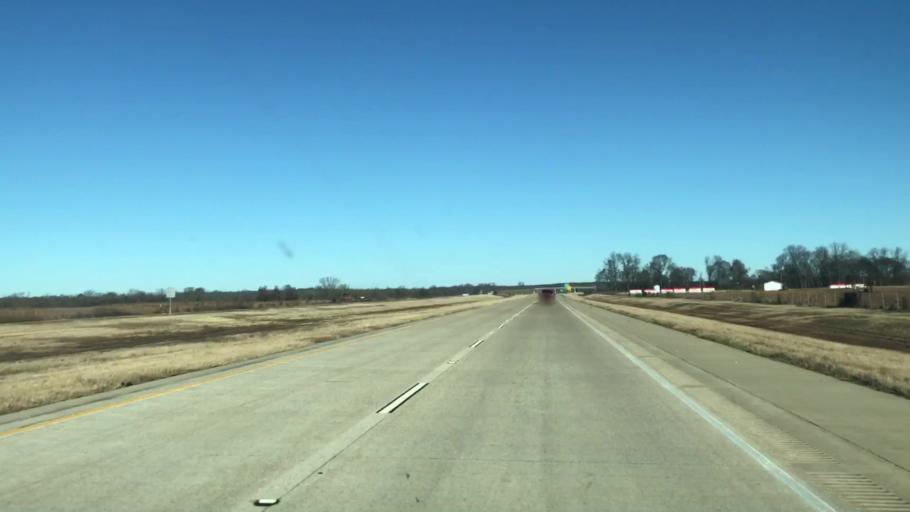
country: US
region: Louisiana
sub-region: Caddo Parish
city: Oil City
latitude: 32.7565
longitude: -93.8841
